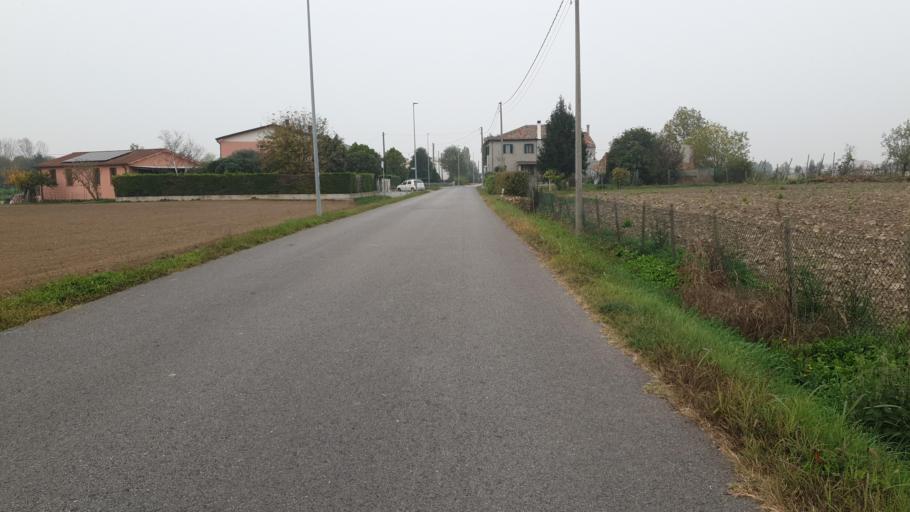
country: IT
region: Veneto
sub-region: Provincia di Padova
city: Bovolenta
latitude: 45.2881
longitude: 11.9190
